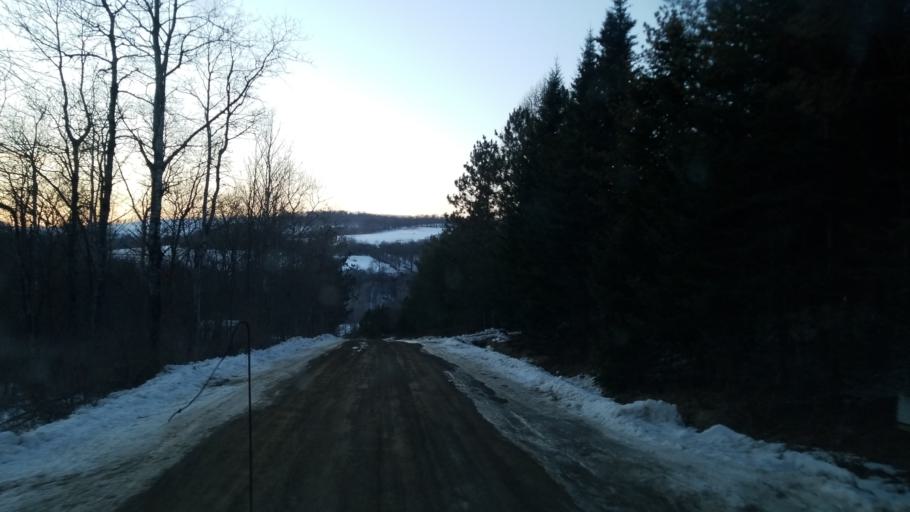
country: US
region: New York
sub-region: Allegany County
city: Andover
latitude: 42.0091
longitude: -77.7558
